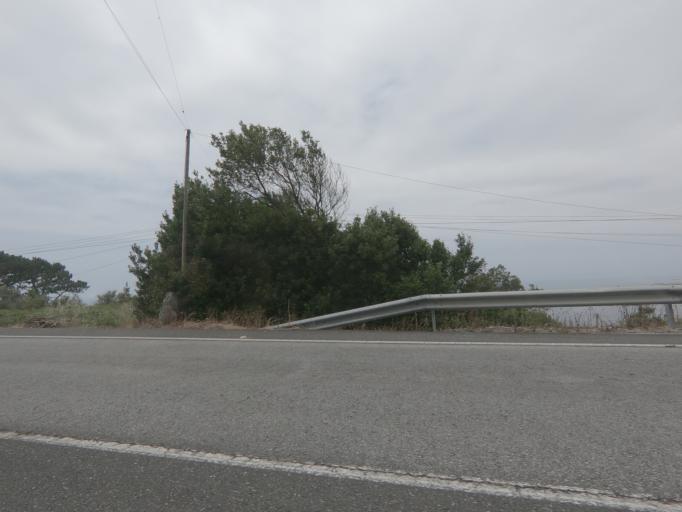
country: ES
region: Galicia
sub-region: Provincia de Pontevedra
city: Oia
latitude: 41.9958
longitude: -8.8780
